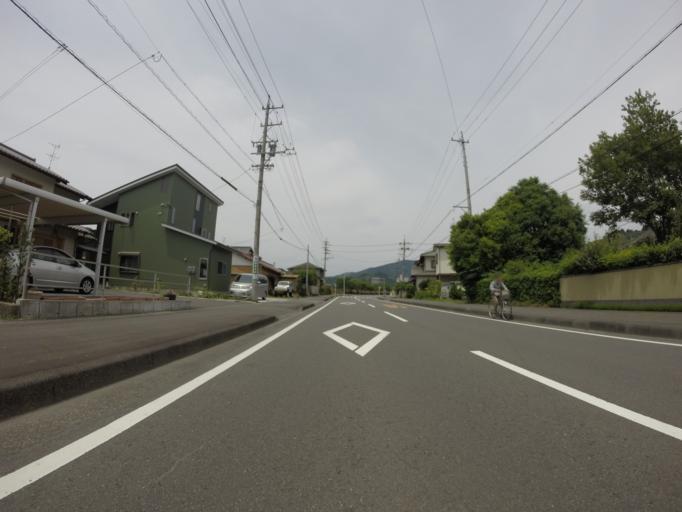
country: JP
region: Shizuoka
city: Shizuoka-shi
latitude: 34.9831
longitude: 138.3186
